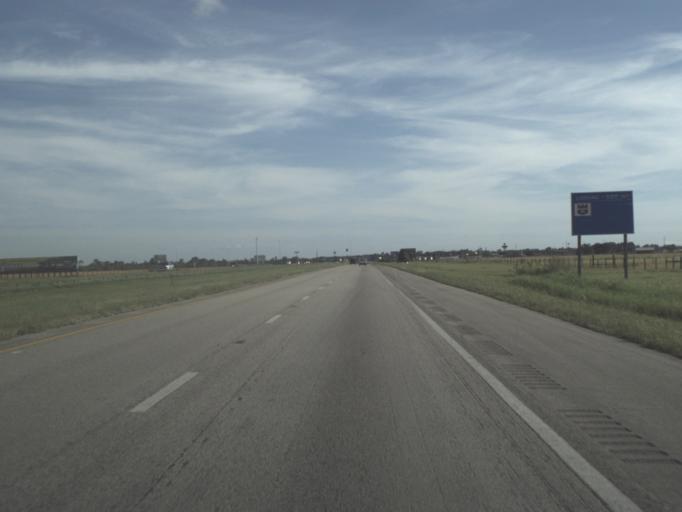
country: US
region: Florida
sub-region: Charlotte County
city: Punta Gorda
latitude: 26.9090
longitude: -82.0102
